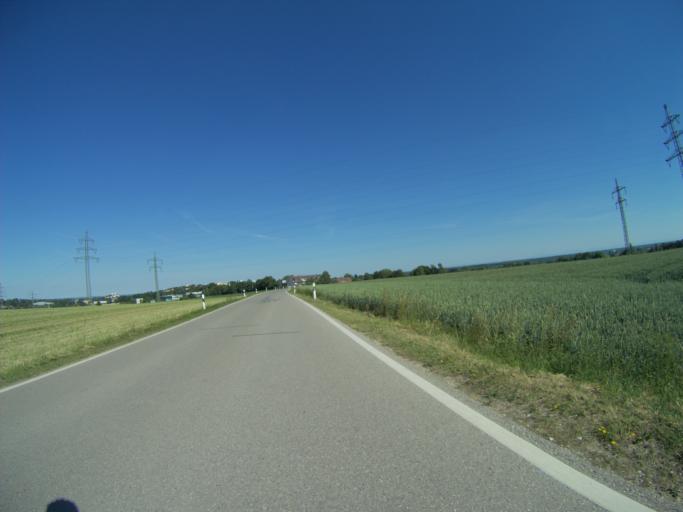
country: DE
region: Bavaria
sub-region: Upper Bavaria
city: Freising
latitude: 48.3994
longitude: 11.7033
